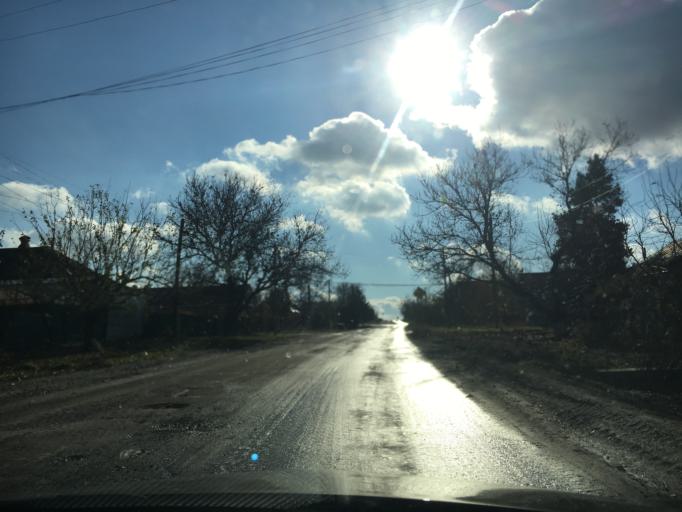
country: RU
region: Rostov
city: Matveyev Kurgan
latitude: 47.5611
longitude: 38.8679
